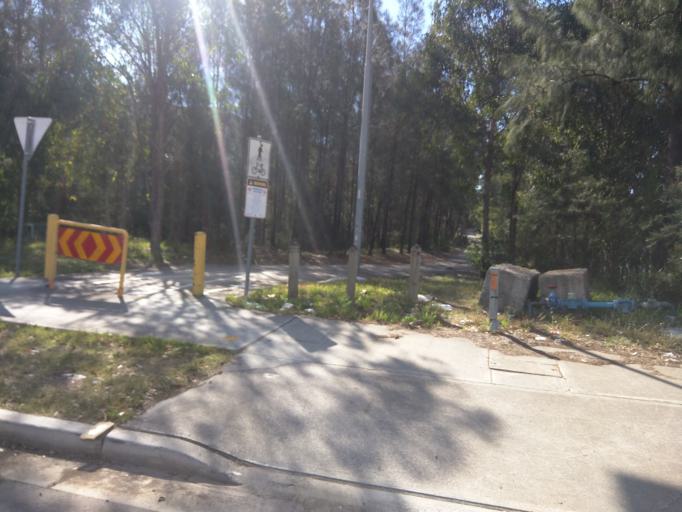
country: AU
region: New South Wales
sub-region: Auburn
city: Auburn
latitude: -33.8364
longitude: 151.0306
